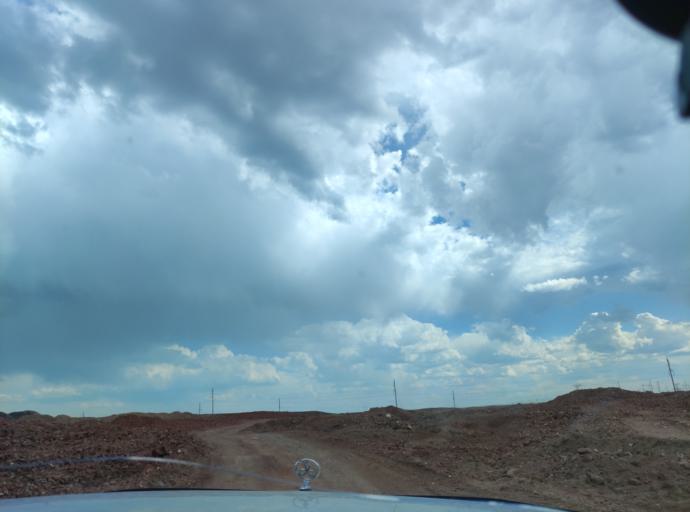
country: KZ
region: Qaraghandy
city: Saryshaghan
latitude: 46.1260
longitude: 73.5965
